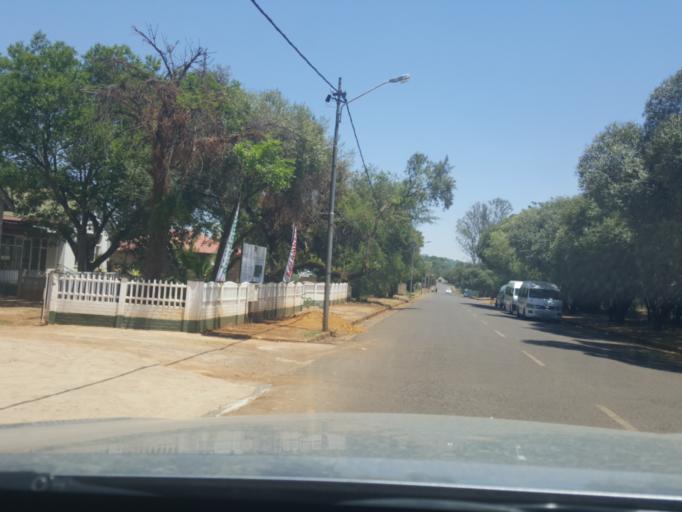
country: ZA
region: North-West
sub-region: Ngaka Modiri Molema District Municipality
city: Zeerust
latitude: -25.5420
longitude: 26.0756
